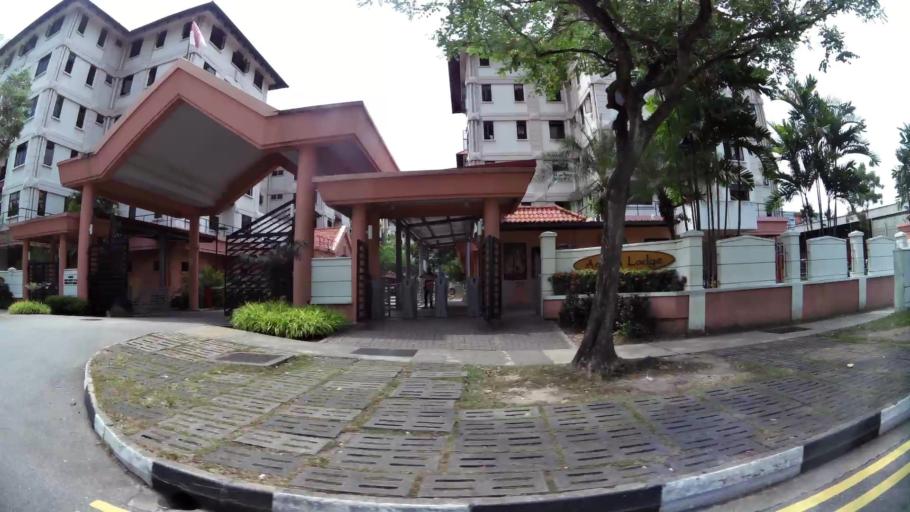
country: SG
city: Singapore
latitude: 1.3404
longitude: 103.7560
